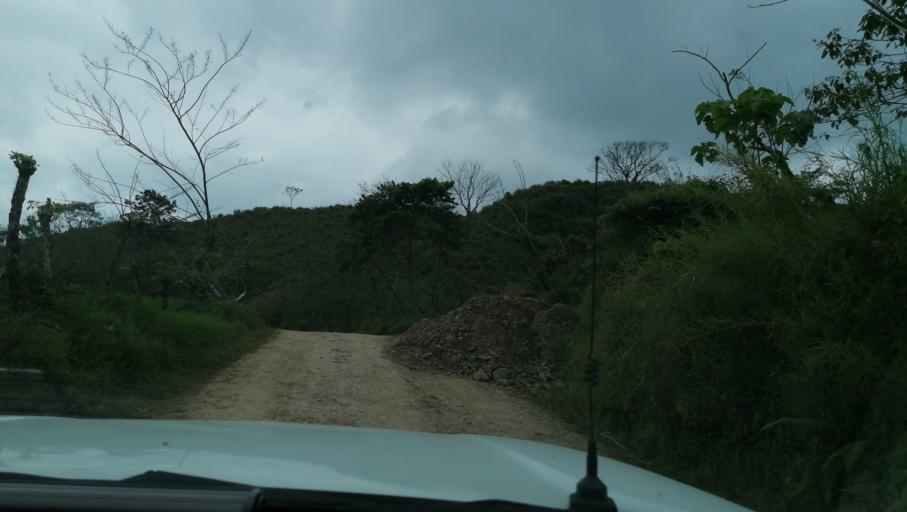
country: MX
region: Chiapas
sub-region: Ocotepec
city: San Pablo Huacano
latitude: 17.2683
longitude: -93.2519
